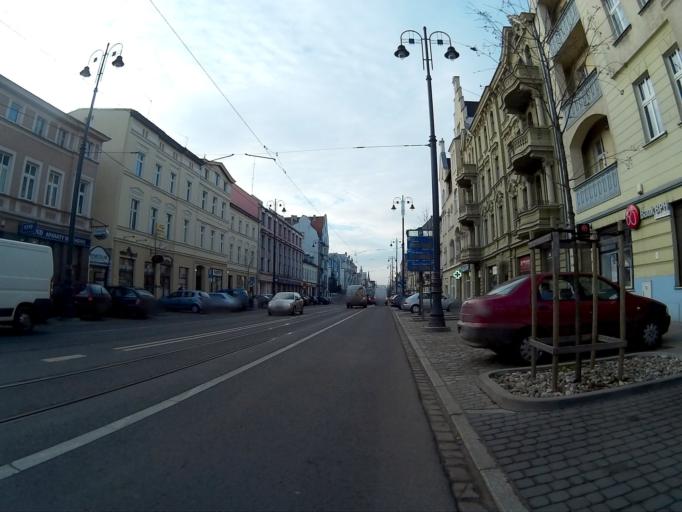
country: PL
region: Kujawsko-Pomorskie
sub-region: Bydgoszcz
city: Bydgoszcz
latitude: 53.1332
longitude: 18.0111
